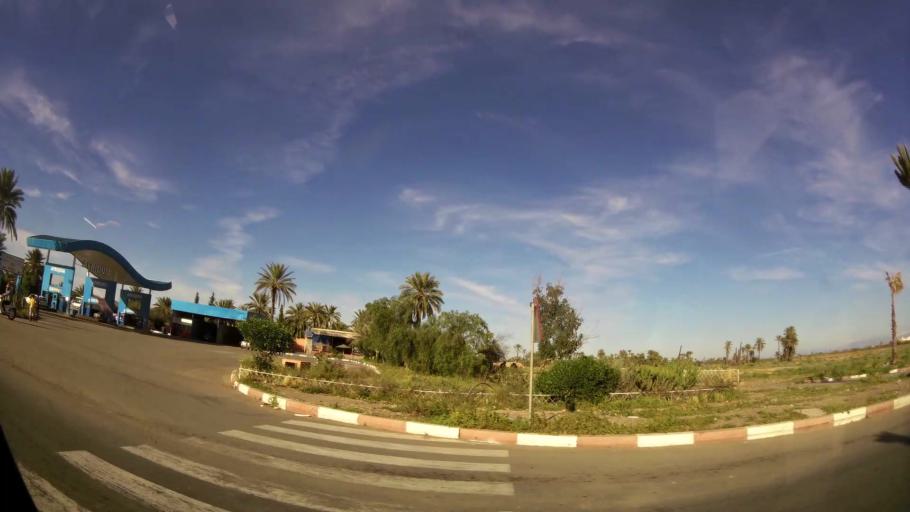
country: MA
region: Marrakech-Tensift-Al Haouz
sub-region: Marrakech
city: Marrakesh
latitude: 31.6926
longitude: -8.0562
